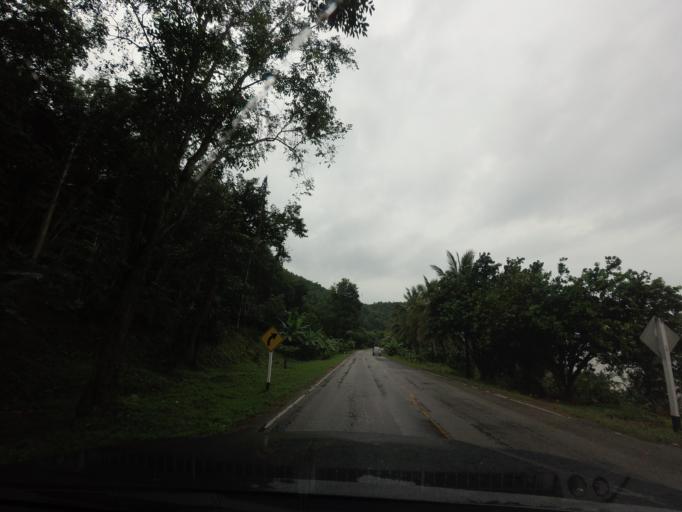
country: TH
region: Nong Khai
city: Sangkhom
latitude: 18.2036
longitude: 102.1517
